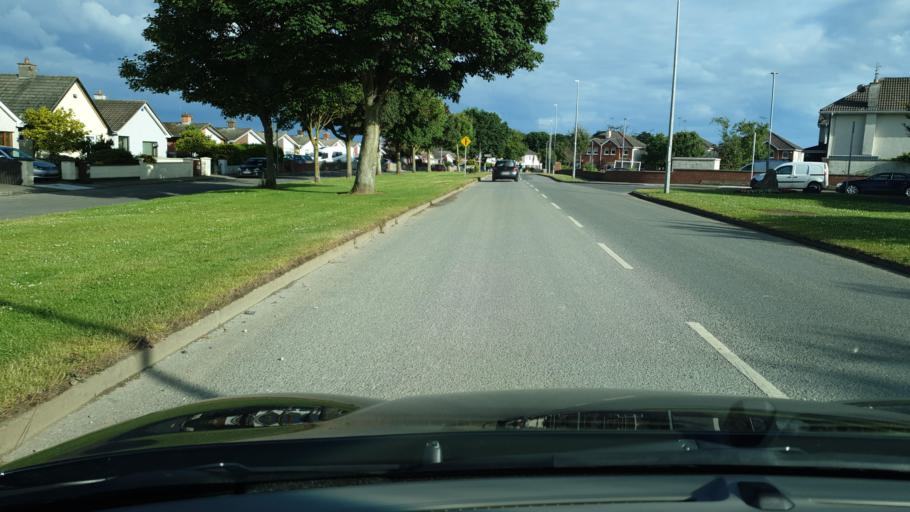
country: IE
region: Leinster
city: An Ros
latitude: 53.5287
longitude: -6.0990
